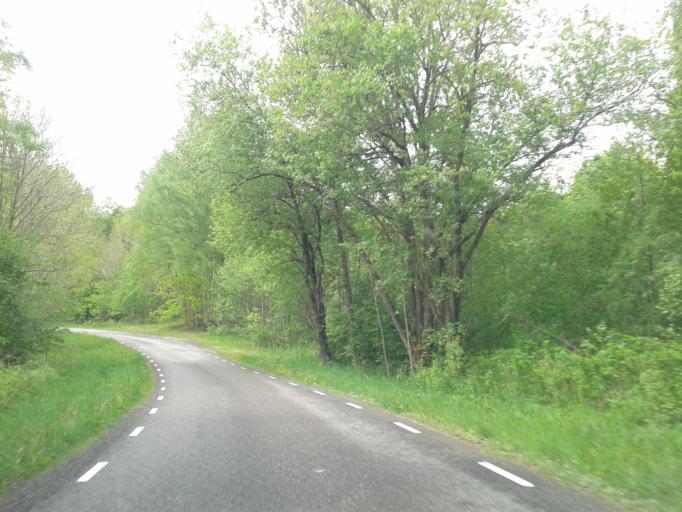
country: SE
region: Vaestra Goetaland
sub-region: Kungalvs Kommun
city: Diserod
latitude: 57.9307
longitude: 11.9538
